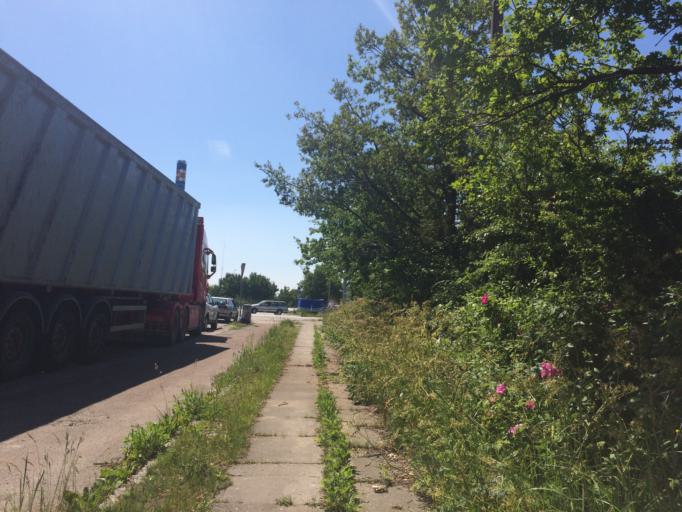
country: DK
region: Capital Region
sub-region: Hvidovre Kommune
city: Hvidovre
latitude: 55.6150
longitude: 12.4693
